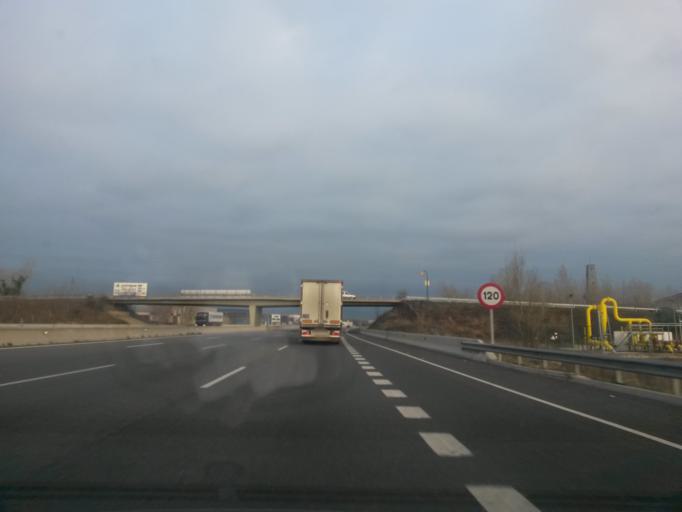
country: ES
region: Catalonia
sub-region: Provincia de Girona
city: Vilablareix
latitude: 41.9637
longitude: 2.7808
